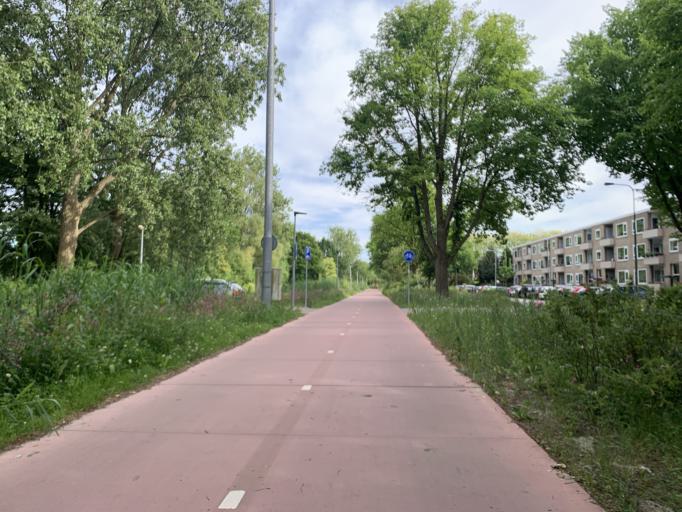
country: NL
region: Groningen
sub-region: Gemeente Groningen
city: Oosterpark
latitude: 53.1990
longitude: 6.5921
